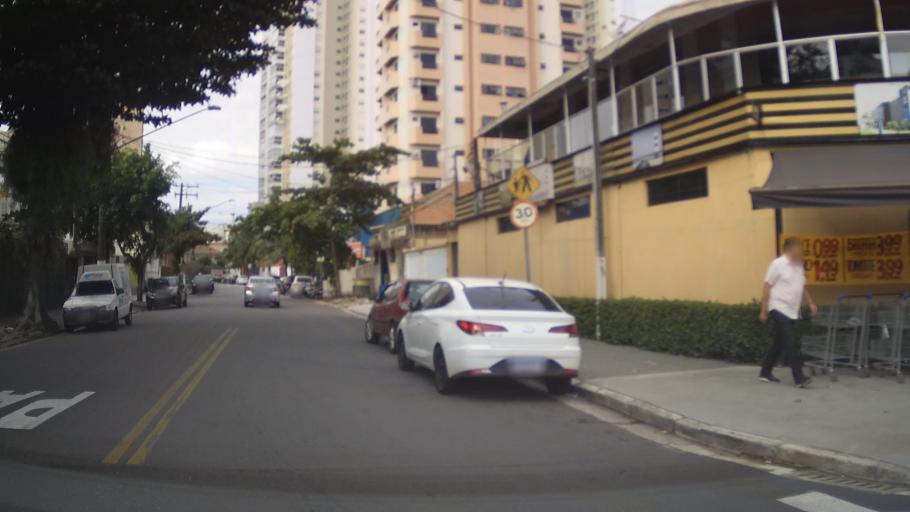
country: BR
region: Sao Paulo
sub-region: Santos
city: Santos
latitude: -23.9834
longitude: -46.2985
